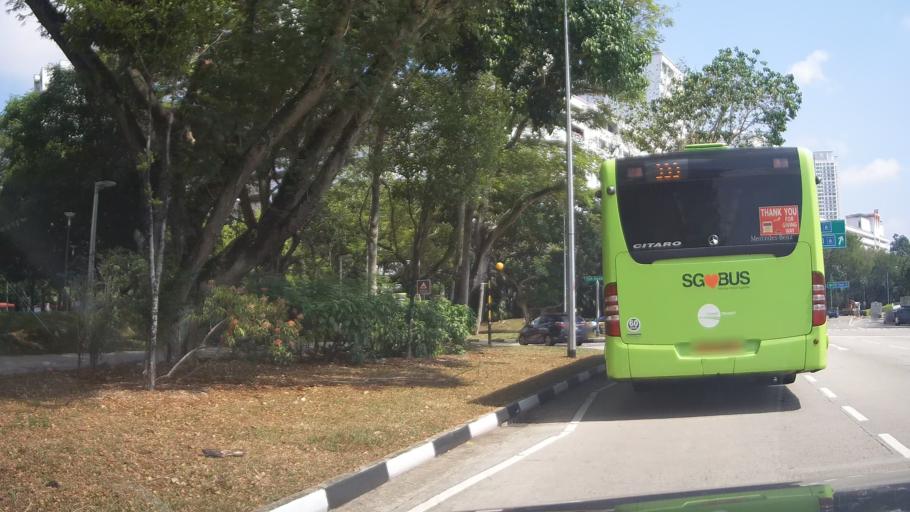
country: SG
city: Singapore
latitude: 1.3383
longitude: 103.7477
